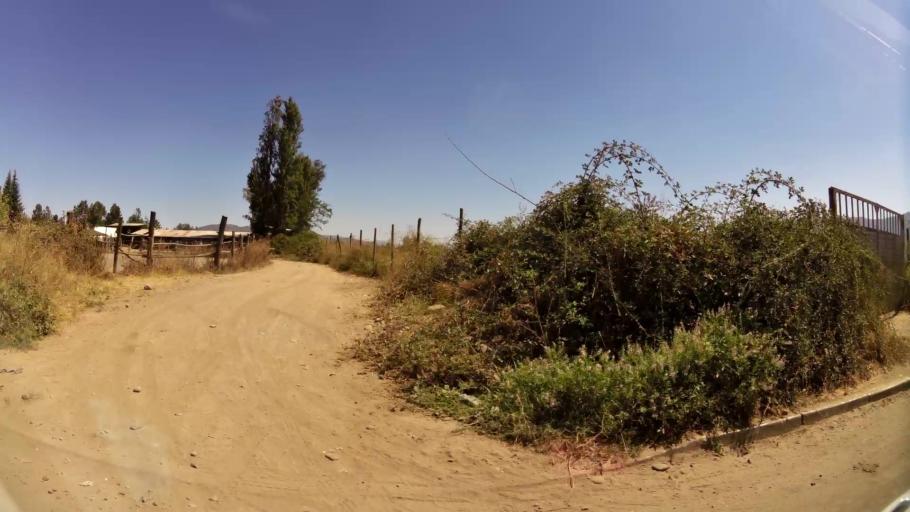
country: CL
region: O'Higgins
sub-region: Provincia de Colchagua
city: Chimbarongo
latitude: -34.5757
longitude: -70.9779
